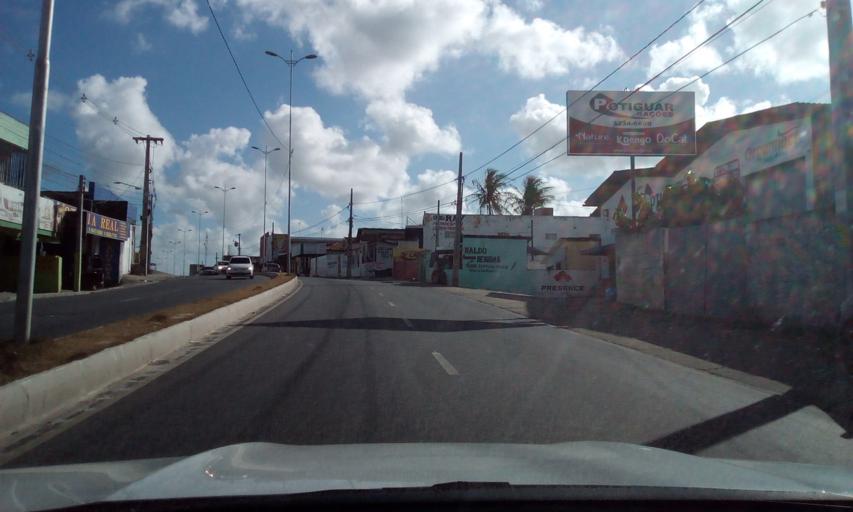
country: BR
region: Paraiba
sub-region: Bayeux
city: Bayeux
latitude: -7.1560
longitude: -34.8960
